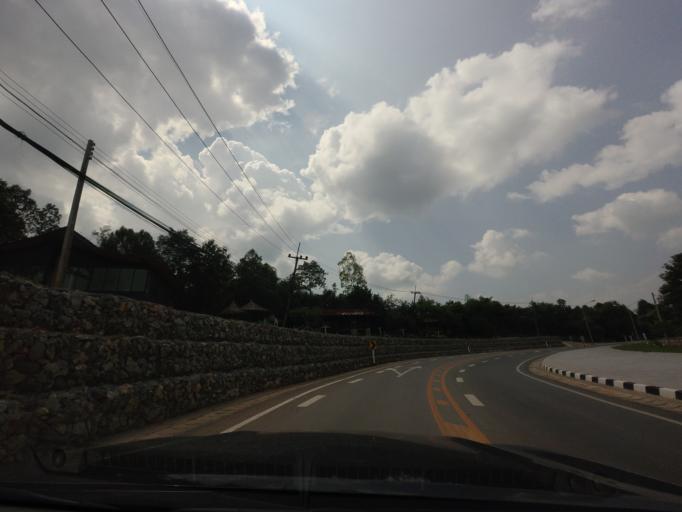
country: TH
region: Nan
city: Pua
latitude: 19.1562
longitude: 100.9301
